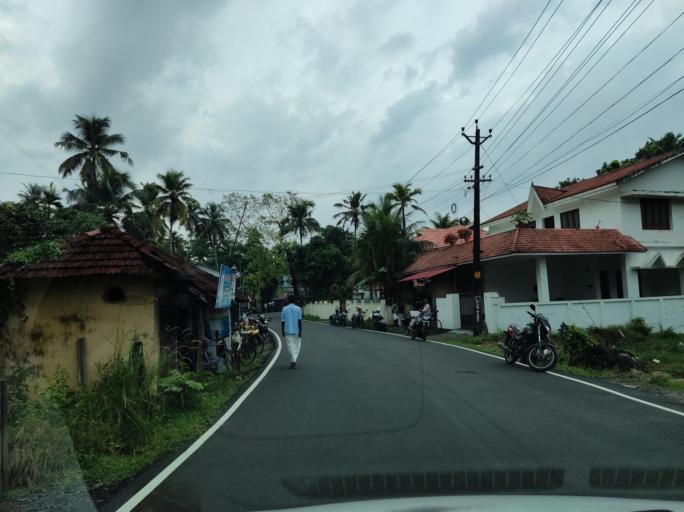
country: IN
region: Kerala
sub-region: Alappuzha
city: Kayankulam
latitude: 9.2654
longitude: 76.4077
